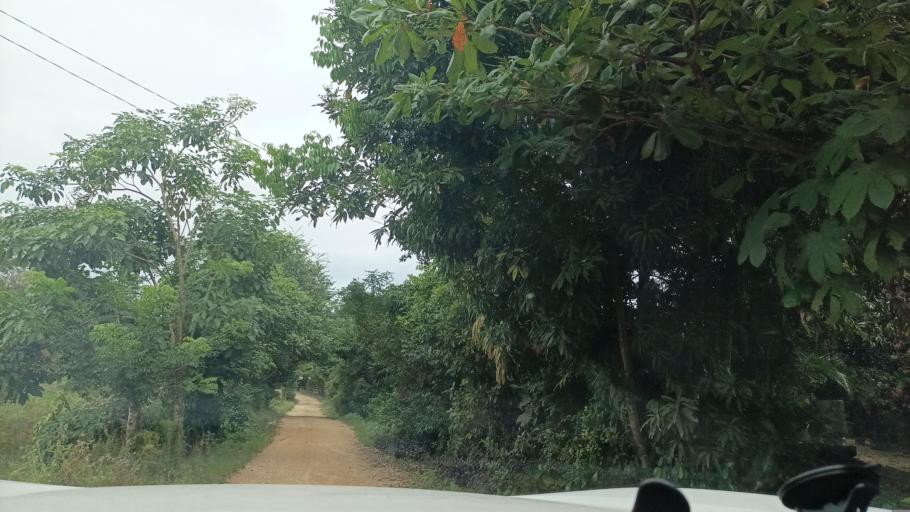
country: MX
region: Veracruz
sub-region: Uxpanapa
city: Poblado Cinco
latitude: 17.4854
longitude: -94.5742
